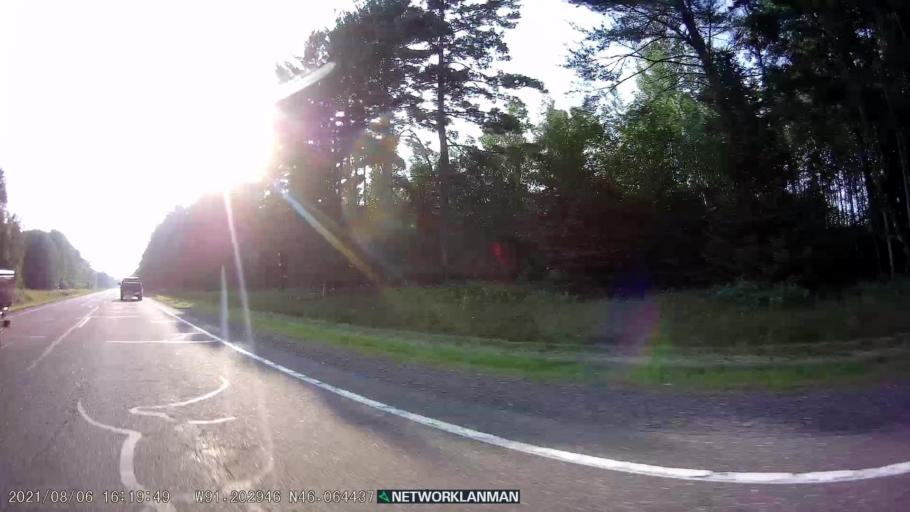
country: US
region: Wisconsin
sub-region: Sawyer County
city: Little Round Lake
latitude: 46.0644
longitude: -91.2022
